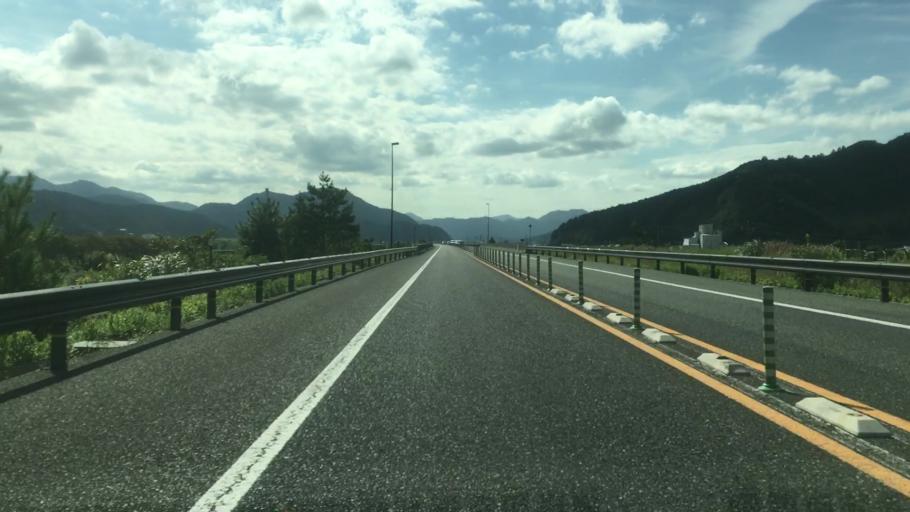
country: JP
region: Kyoto
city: Fukuchiyama
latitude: 35.2143
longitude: 135.0358
